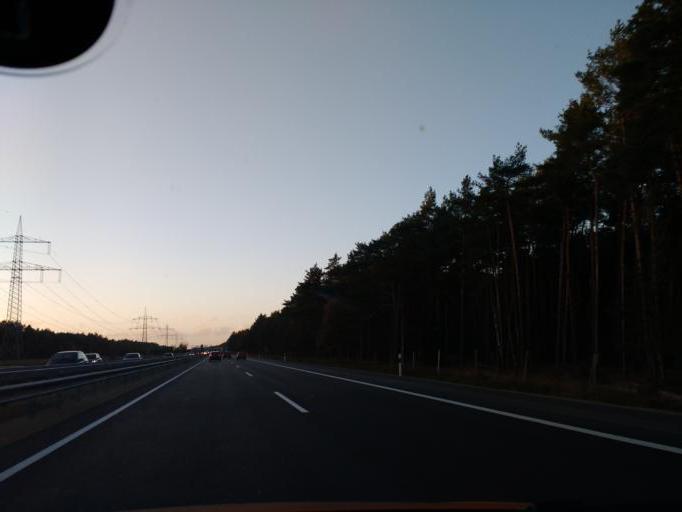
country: DE
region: Schleswig-Holstein
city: Gudow
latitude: 53.5231
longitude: 10.7955
